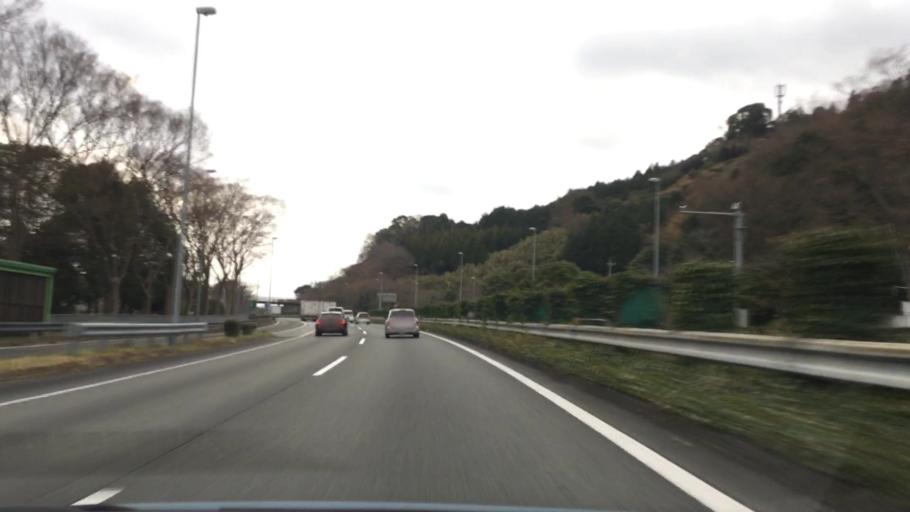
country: JP
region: Shizuoka
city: Fujinomiya
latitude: 35.1581
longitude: 138.6181
